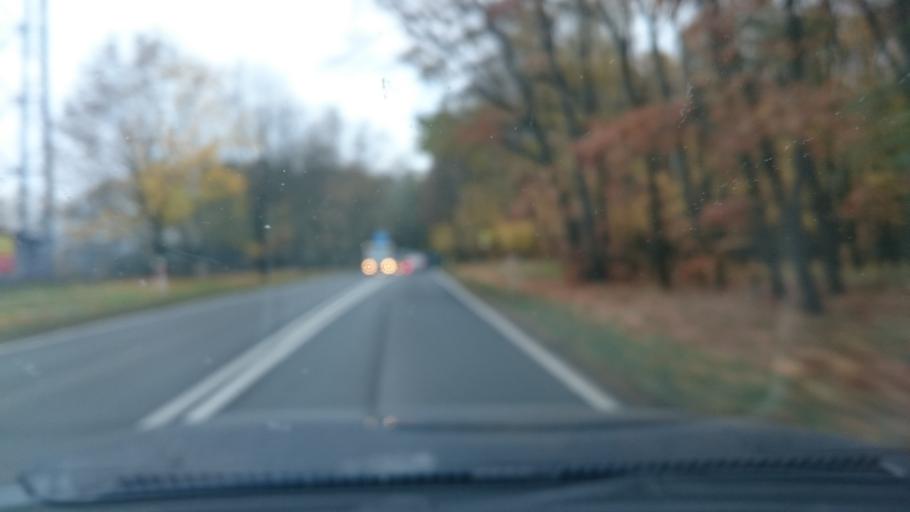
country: PL
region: Silesian Voivodeship
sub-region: Rybnik
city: Rybnik
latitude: 50.1084
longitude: 18.5807
